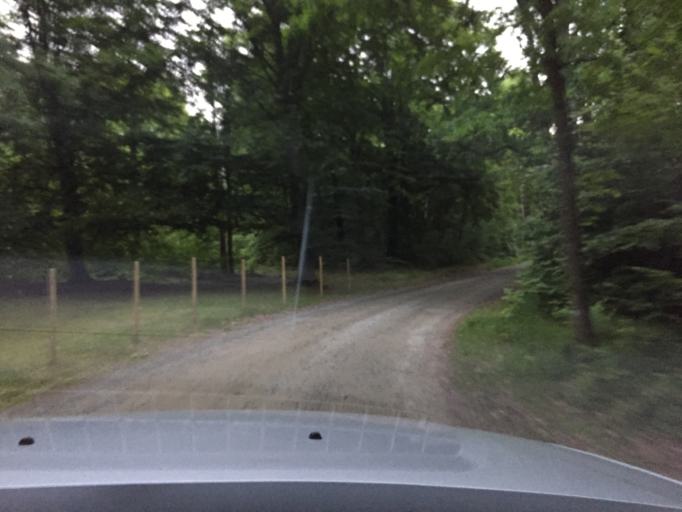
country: SE
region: Skane
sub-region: Kristianstads Kommun
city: Degeberga
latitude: 55.7310
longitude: 14.1232
